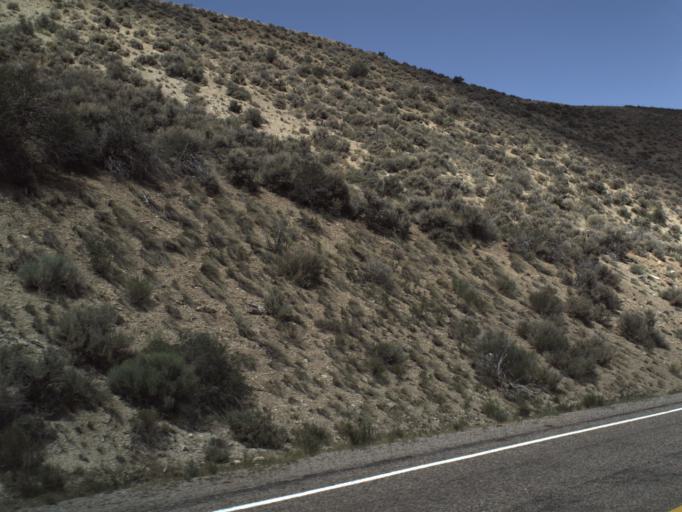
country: US
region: Utah
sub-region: Rich County
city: Randolph
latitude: 41.4969
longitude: -111.3241
